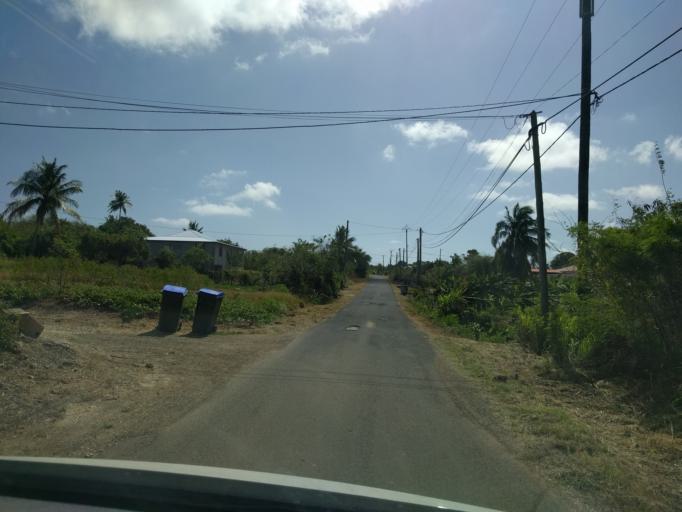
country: GP
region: Guadeloupe
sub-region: Guadeloupe
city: Grand-Bourg
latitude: 15.9780
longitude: -61.2502
